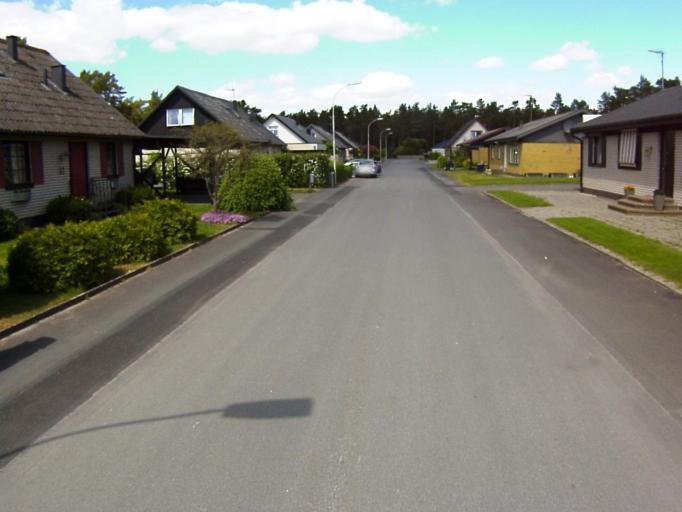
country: SE
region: Skane
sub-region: Kristianstads Kommun
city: Ahus
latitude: 55.9468
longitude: 14.2724
